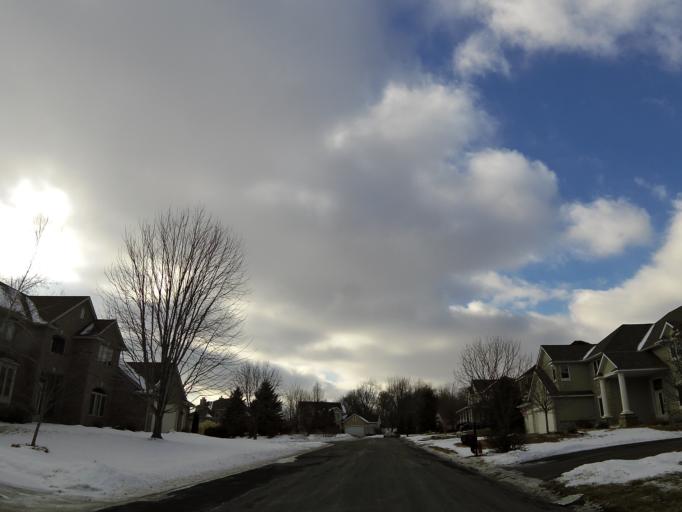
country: US
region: Minnesota
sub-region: Scott County
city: Prior Lake
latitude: 44.7316
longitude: -93.4549
